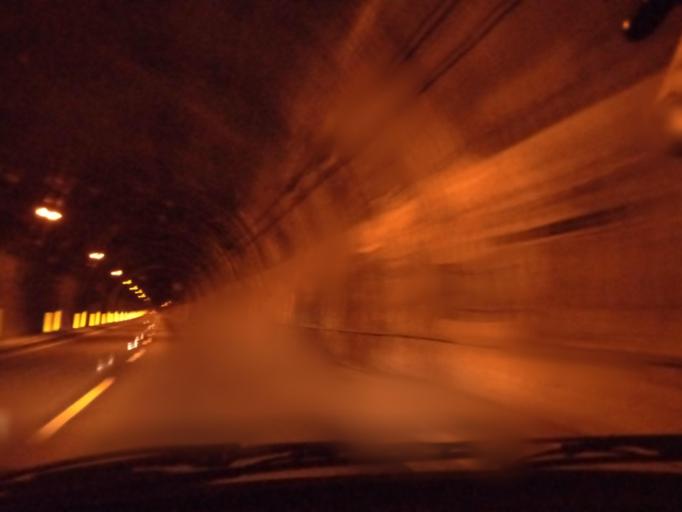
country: IT
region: Sicily
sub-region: Messina
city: Piraino
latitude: 38.1402
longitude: 14.8750
